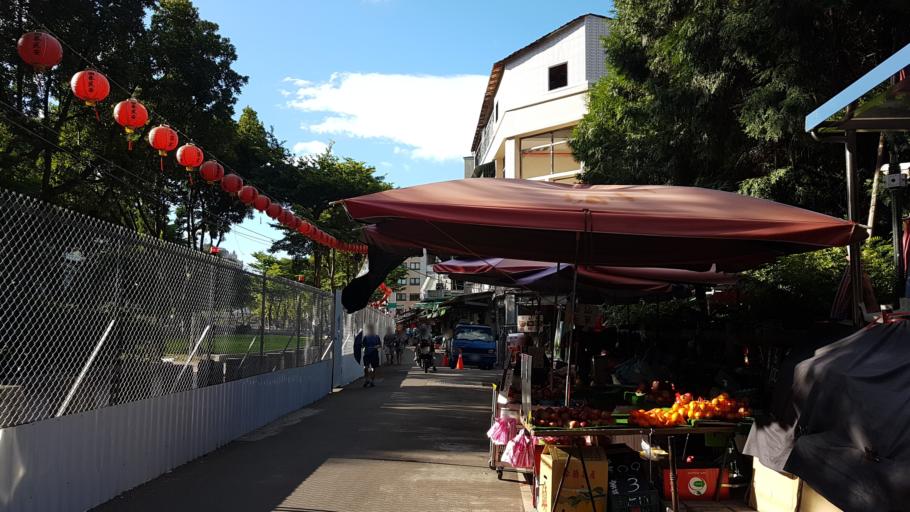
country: TW
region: Taipei
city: Taipei
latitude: 25.0593
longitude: 121.5209
